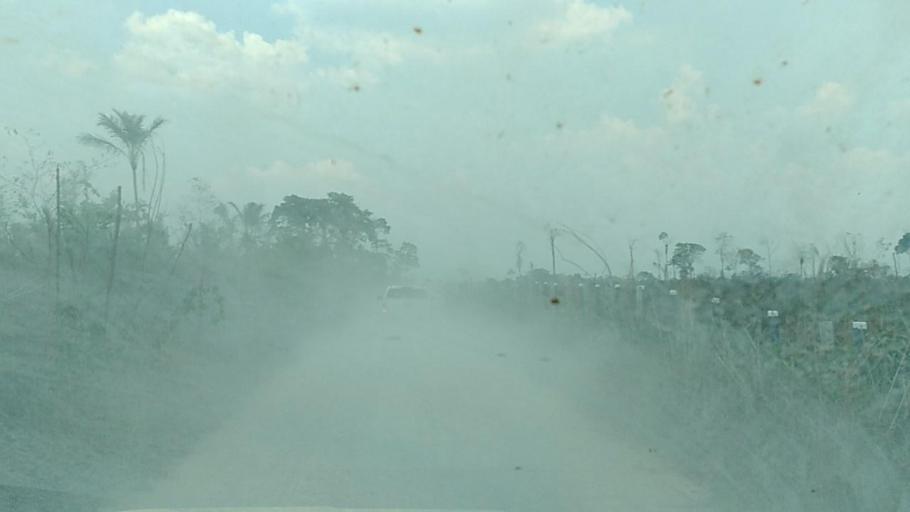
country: BR
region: Rondonia
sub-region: Porto Velho
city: Porto Velho
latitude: -8.7730
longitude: -63.2118
